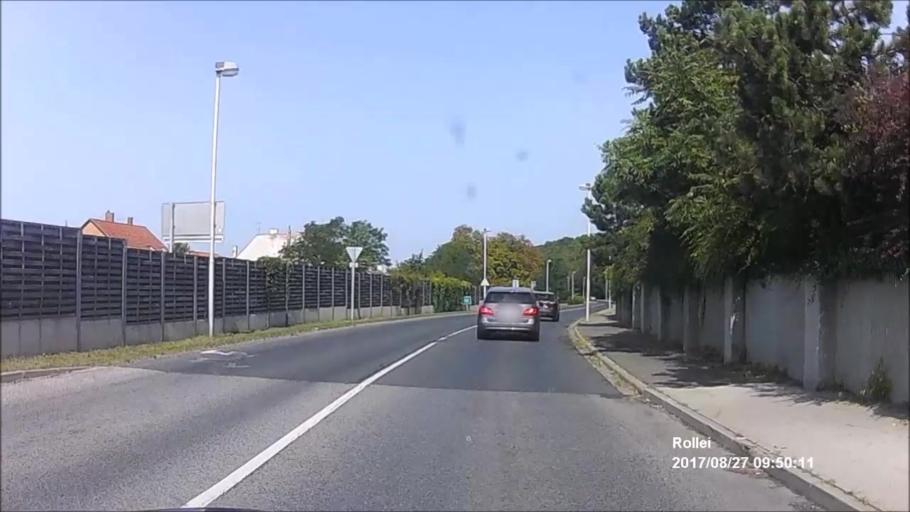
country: HU
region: Gyor-Moson-Sopron
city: Sopron
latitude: 47.6919
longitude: 16.5894
